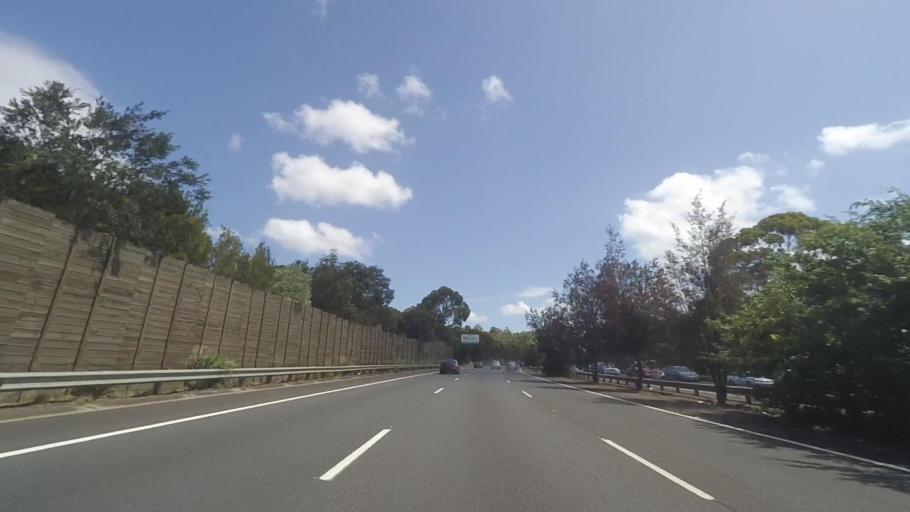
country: AU
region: New South Wales
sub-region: Hornsby Shire
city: Mount Colah
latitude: -33.6935
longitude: 151.1216
